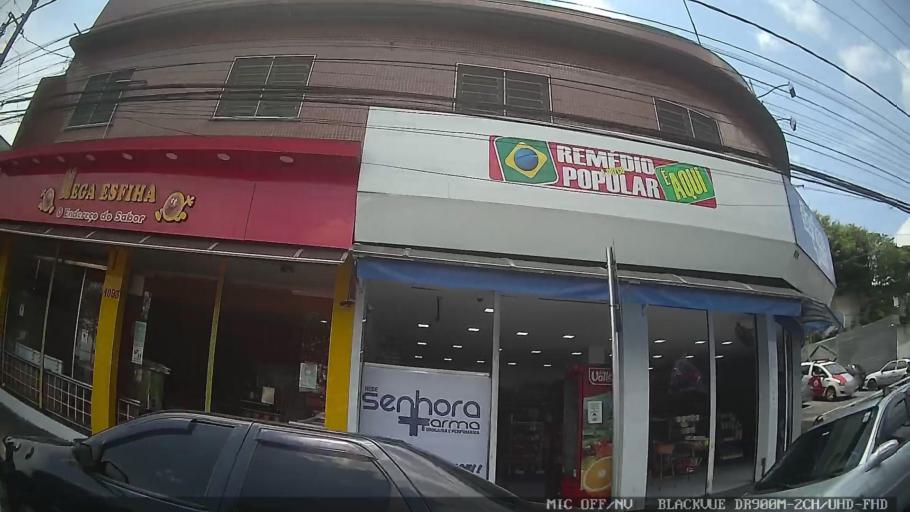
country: BR
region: Sao Paulo
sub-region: Ferraz De Vasconcelos
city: Ferraz de Vasconcelos
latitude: -23.5548
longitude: -46.3830
